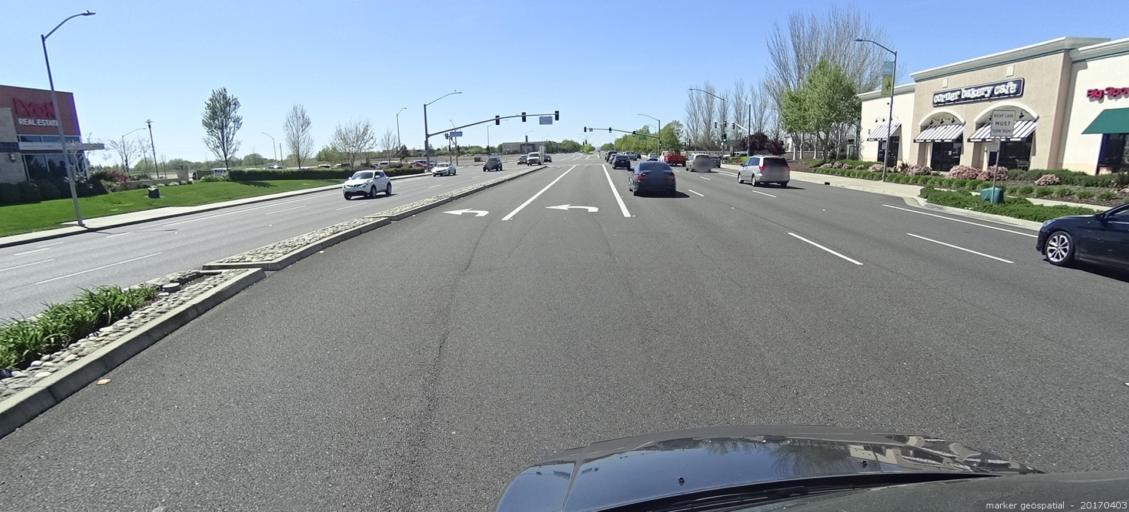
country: US
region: California
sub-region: Sacramento County
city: Rio Linda
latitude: 38.6561
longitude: -121.5108
